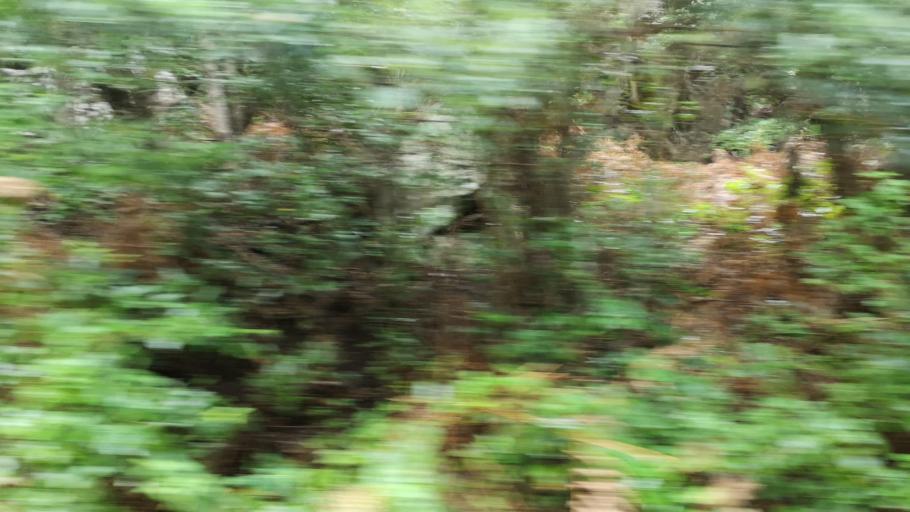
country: ES
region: Canary Islands
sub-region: Provincia de Santa Cruz de Tenerife
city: Vallehermosa
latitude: 28.1629
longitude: -17.2954
